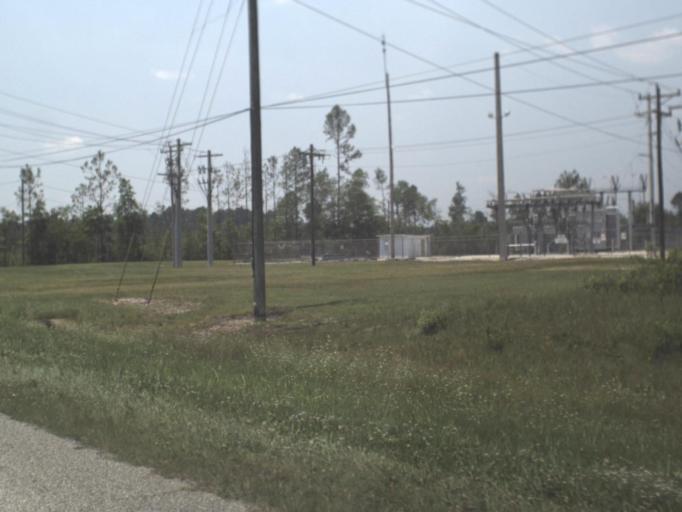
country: US
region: Florida
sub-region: Duval County
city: Baldwin
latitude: 30.1831
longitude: -82.0220
